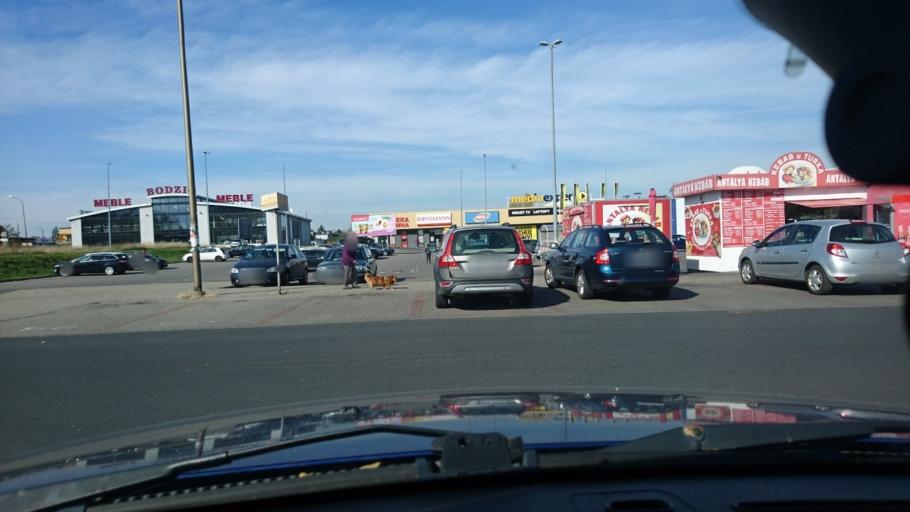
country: PL
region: Silesian Voivodeship
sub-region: Myslowice
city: Myslowice
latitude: 50.2363
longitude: 19.1272
